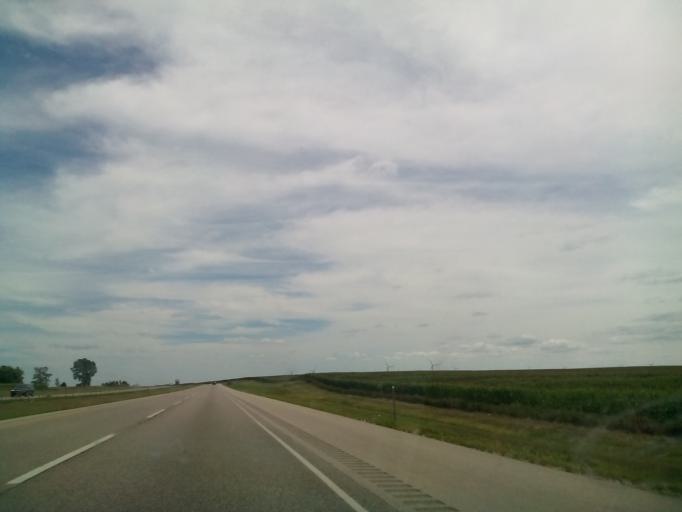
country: US
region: Illinois
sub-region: DeKalb County
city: Malta
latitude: 41.9013
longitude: -88.9588
